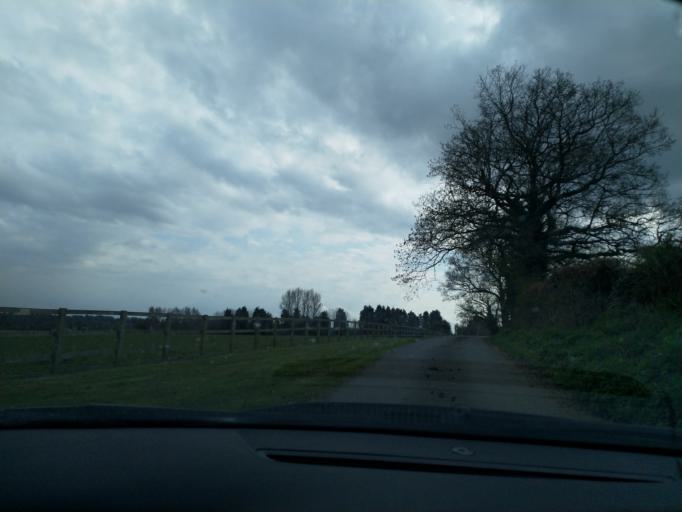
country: GB
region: England
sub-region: Warwickshire
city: Wroxall
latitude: 52.2930
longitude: -1.6874
